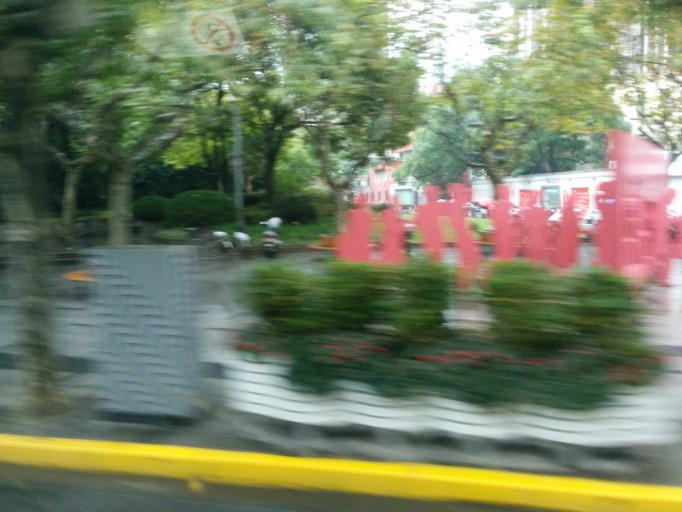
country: CN
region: Shanghai Shi
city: Shanghai
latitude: 31.2327
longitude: 121.4595
